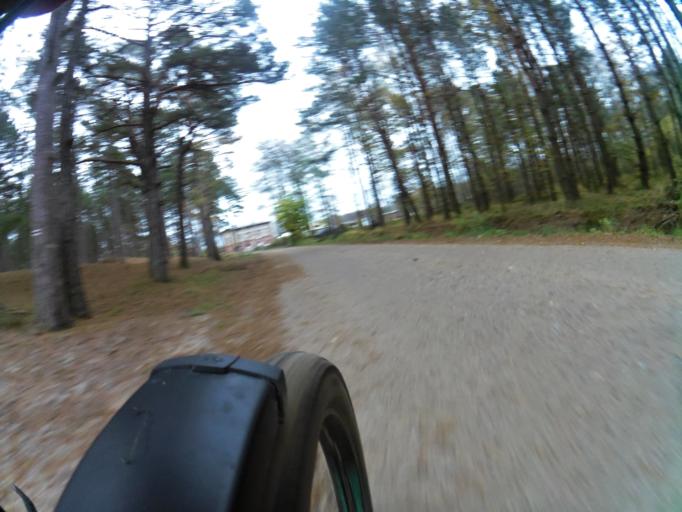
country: PL
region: Pomeranian Voivodeship
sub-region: Powiat wejherowski
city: Choczewo
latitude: 54.7813
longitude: 17.7365
